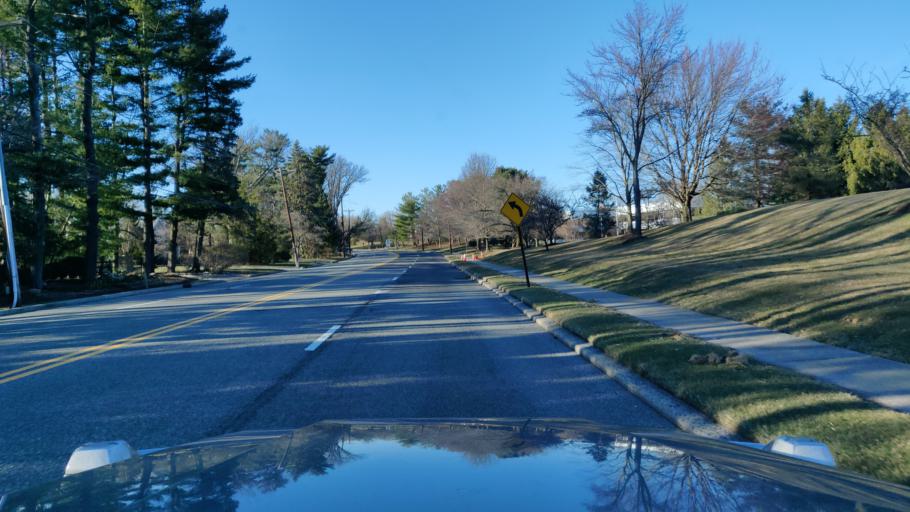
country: US
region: New Jersey
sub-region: Bergen County
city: Woodcliff Lake
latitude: 41.0332
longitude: -74.0739
